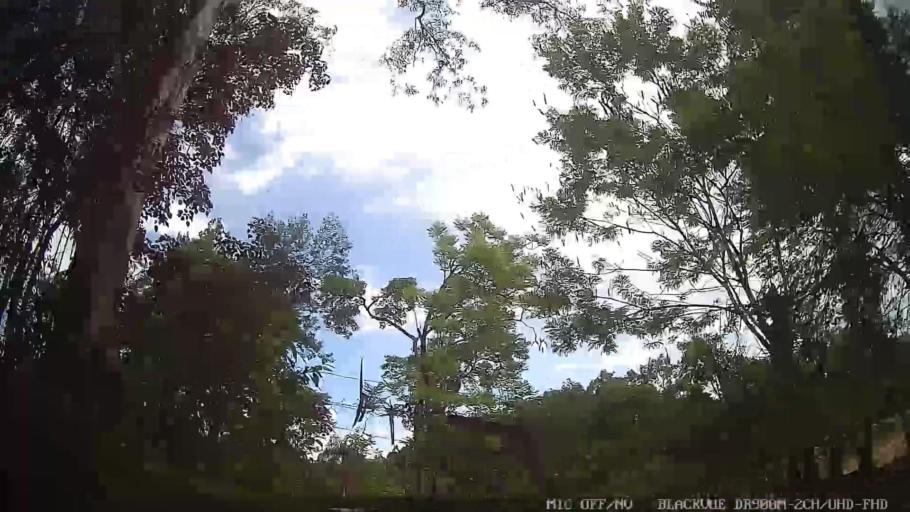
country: BR
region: Sao Paulo
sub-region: Serra Negra
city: Serra Negra
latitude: -22.6148
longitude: -46.7385
